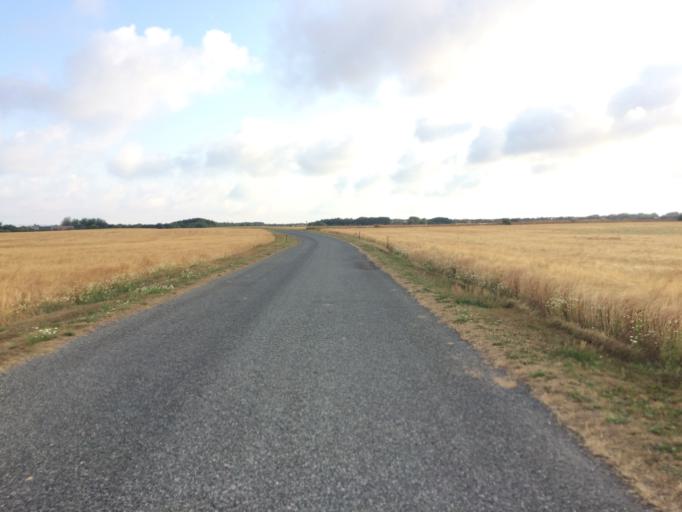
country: DK
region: Central Jutland
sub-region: Holstebro Kommune
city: Vinderup
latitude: 56.6044
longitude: 8.7193
